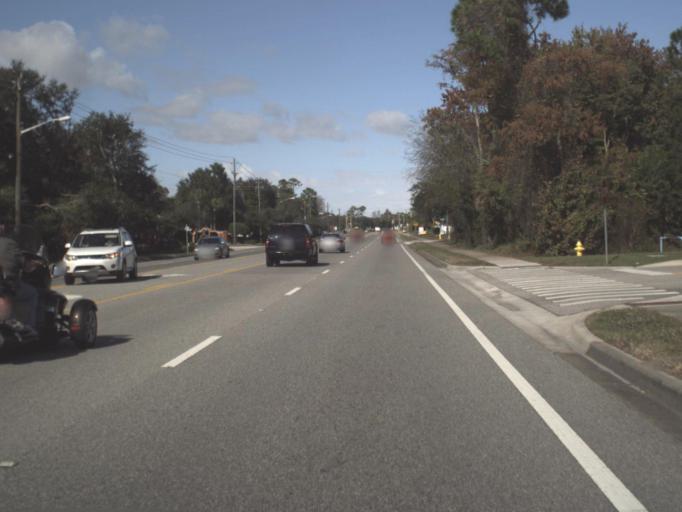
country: US
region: Florida
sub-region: Volusia County
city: South Daytona
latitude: 29.1455
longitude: -81.0351
